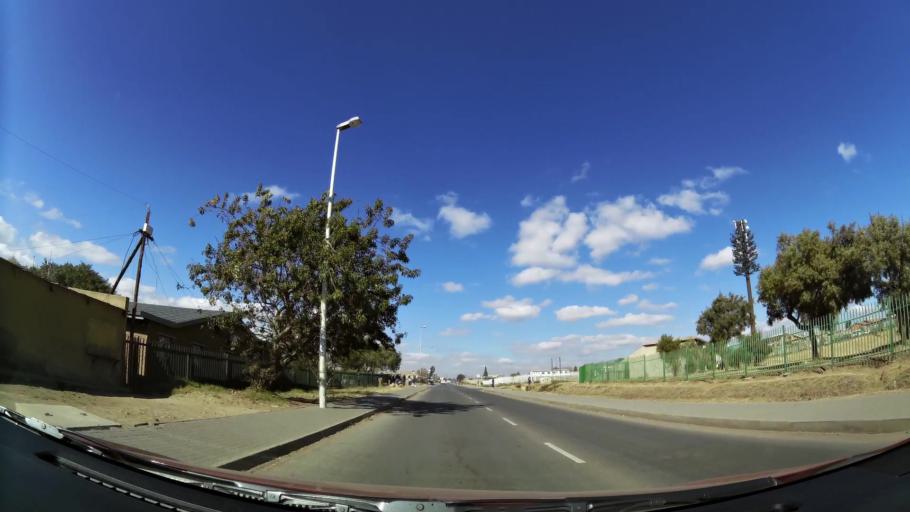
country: ZA
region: Gauteng
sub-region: City of Johannesburg Metropolitan Municipality
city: Modderfontein
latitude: -26.0440
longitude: 28.1815
